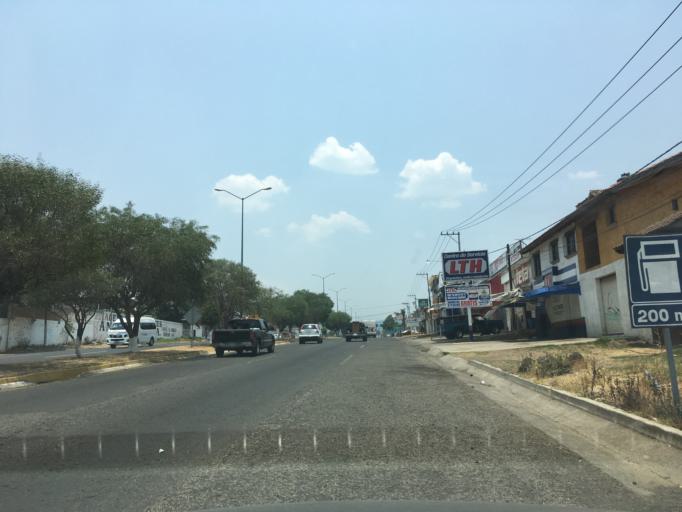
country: MX
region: Michoacan
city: Patzcuaro
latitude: 19.5192
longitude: -101.6169
